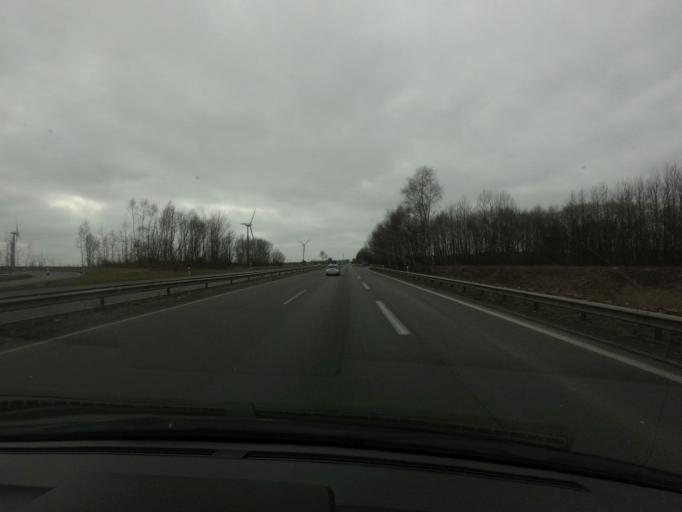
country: DE
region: Lower Saxony
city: Seevetal
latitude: 53.4016
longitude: 9.9037
